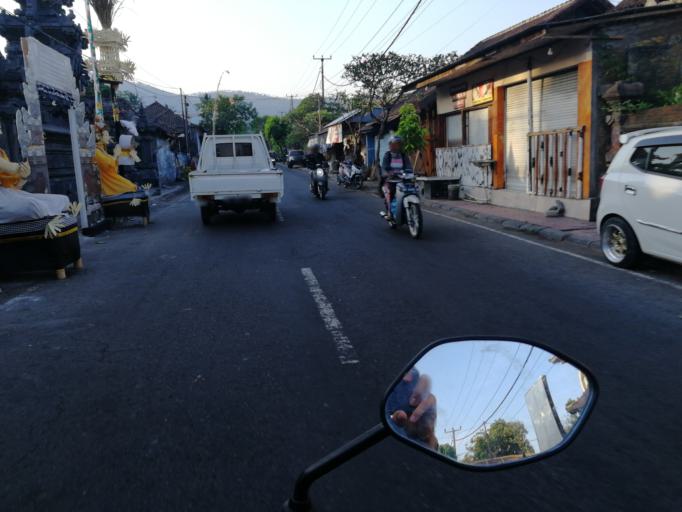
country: ID
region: Bali
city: Banjar Buayang
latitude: -8.3464
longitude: 115.6146
